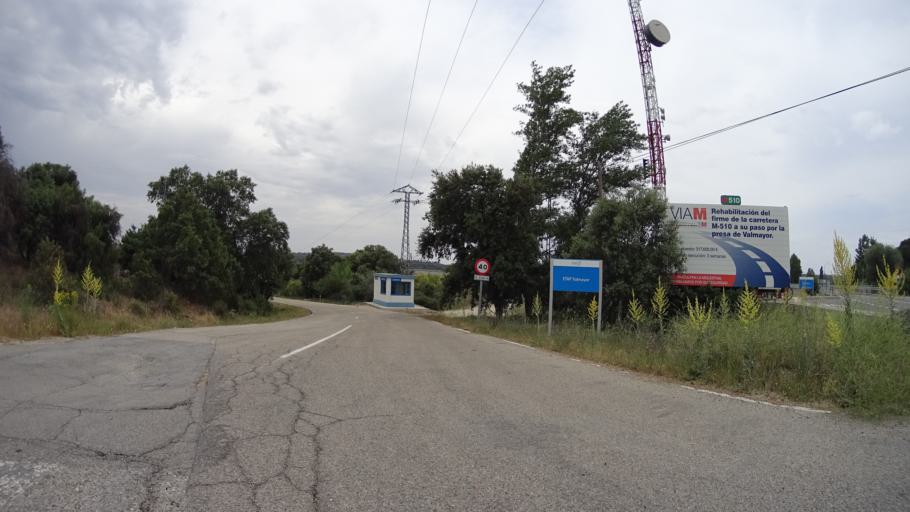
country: ES
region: Madrid
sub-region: Provincia de Madrid
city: Colmenarejo
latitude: 40.5414
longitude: -4.0452
